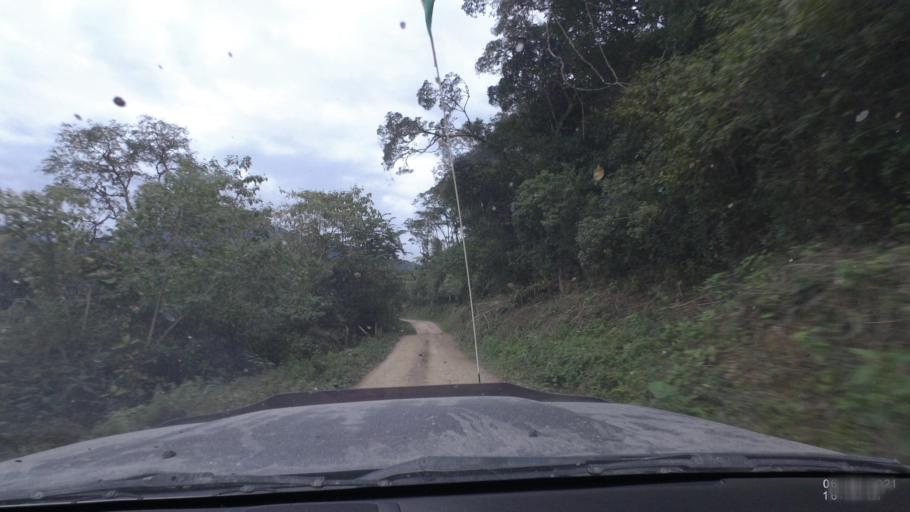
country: BO
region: La Paz
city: Quime
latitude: -16.5282
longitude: -66.7623
